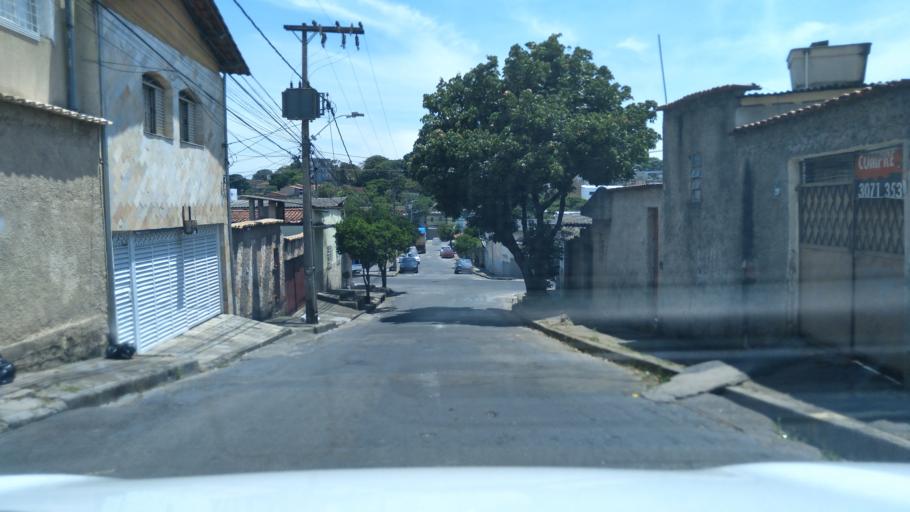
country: BR
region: Minas Gerais
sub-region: Contagem
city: Contagem
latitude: -19.8995
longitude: -44.0110
